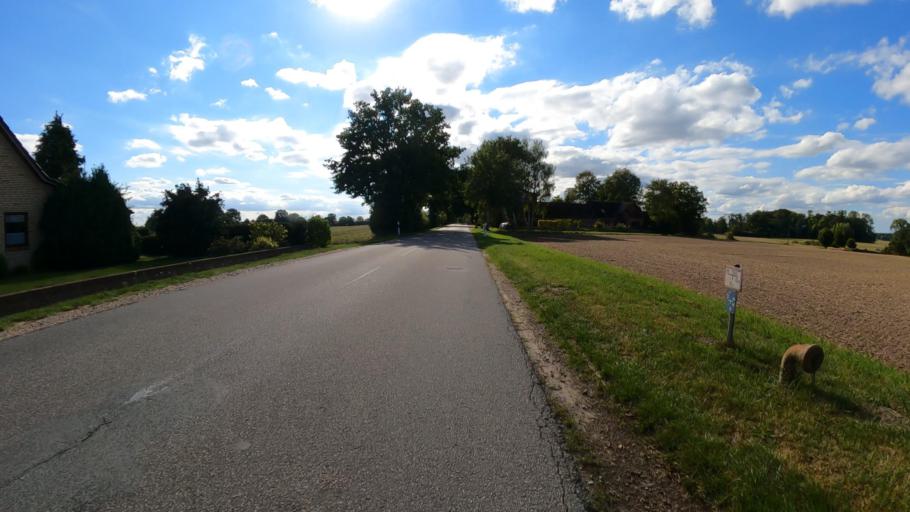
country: DE
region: Schleswig-Holstein
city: Todendorf
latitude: 53.6994
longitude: 10.3613
